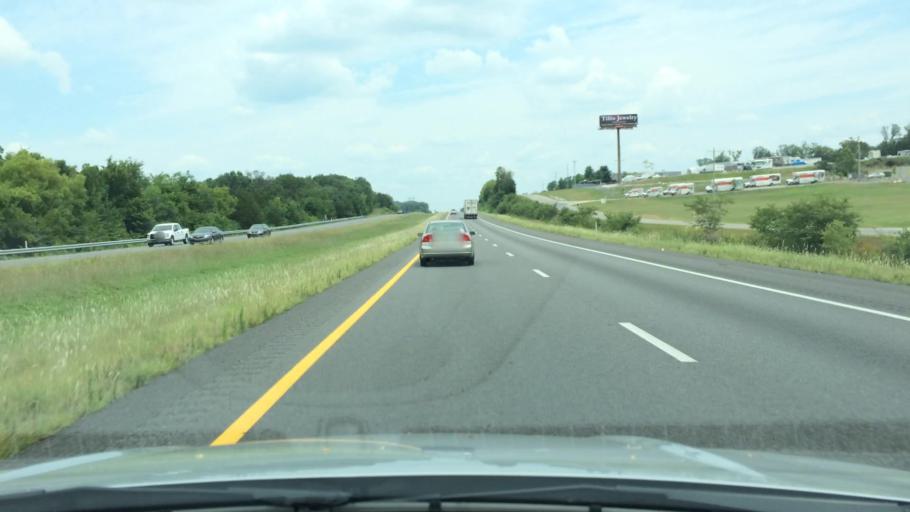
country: US
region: Tennessee
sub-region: Maury County
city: Spring Hill
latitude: 35.6967
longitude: -86.8838
